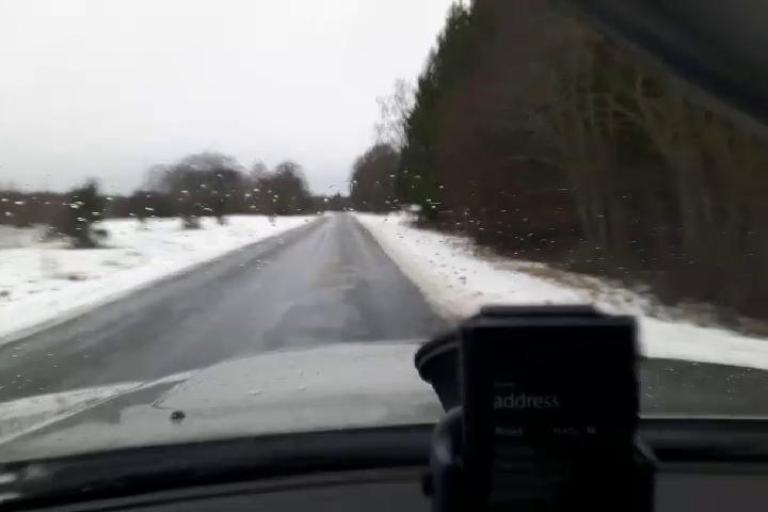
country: EE
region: Harju
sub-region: Harku vald
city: Tabasalu
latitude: 59.4290
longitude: 24.4339
